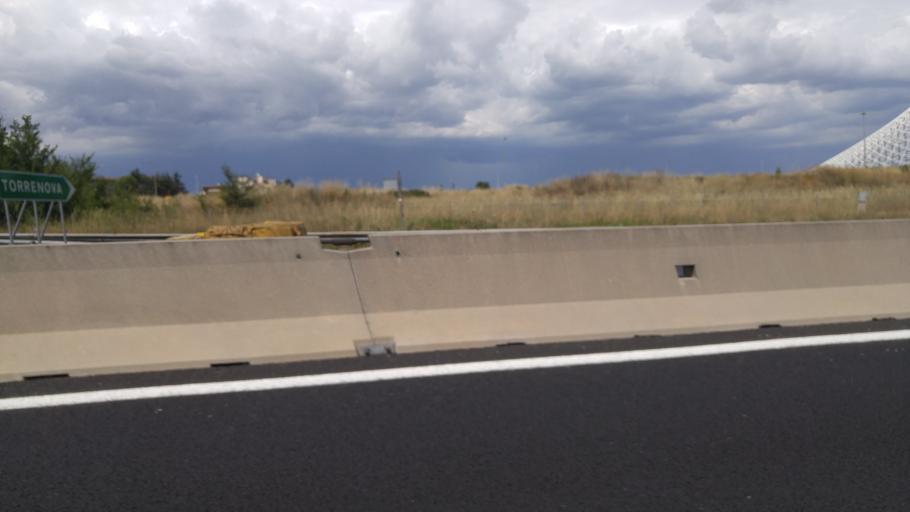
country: IT
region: Latium
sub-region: Citta metropolitana di Roma Capitale
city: Frascati
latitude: 41.8414
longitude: 12.6297
